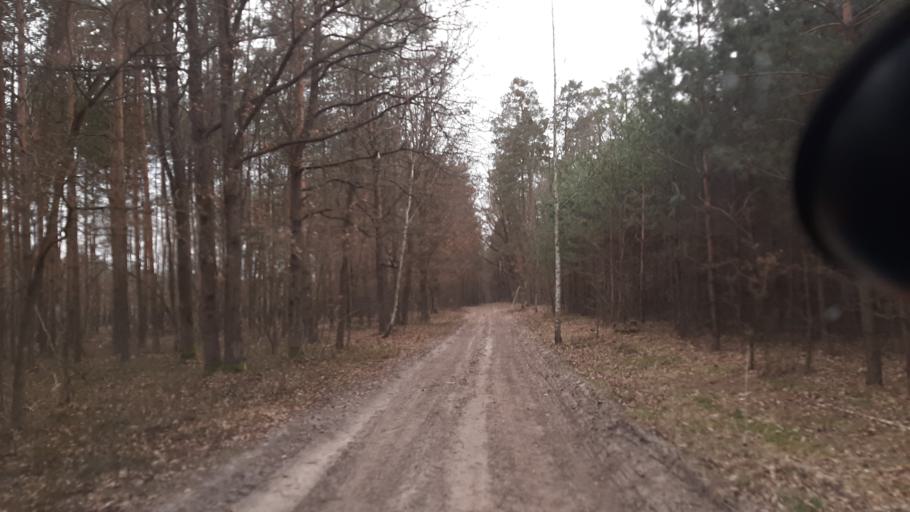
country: PL
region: Lublin Voivodeship
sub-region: Powiat lubelski
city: Garbow
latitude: 51.4017
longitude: 22.3689
